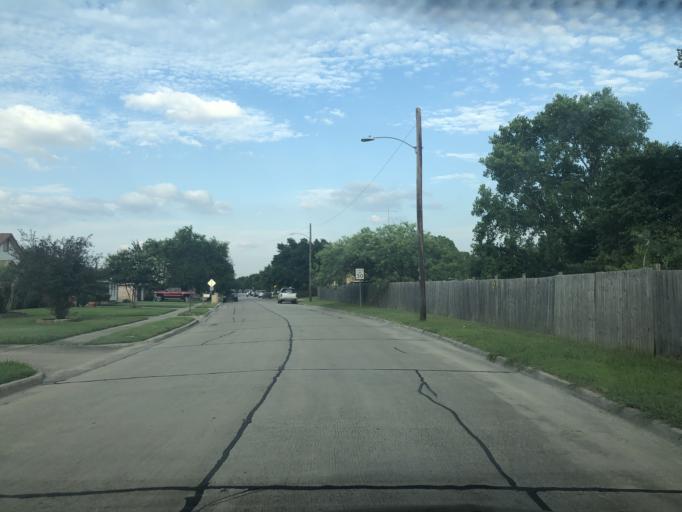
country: US
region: Texas
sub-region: Dallas County
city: Irving
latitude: 32.7909
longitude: -96.9519
